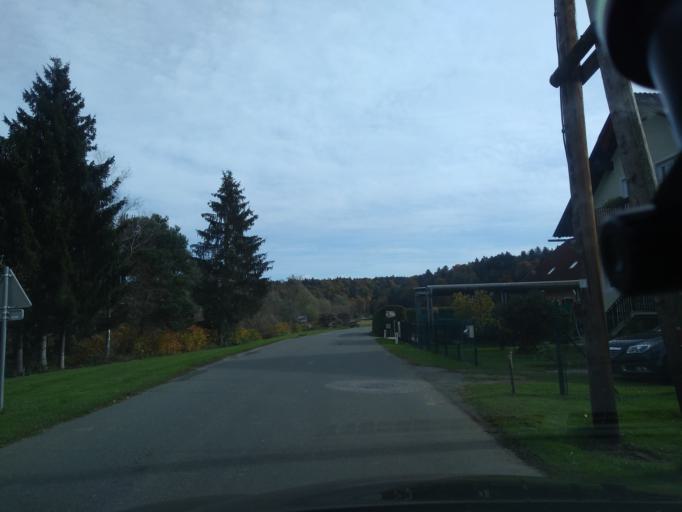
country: AT
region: Styria
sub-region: Politischer Bezirk Leibnitz
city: Heimschuh
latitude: 46.7581
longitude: 15.4922
